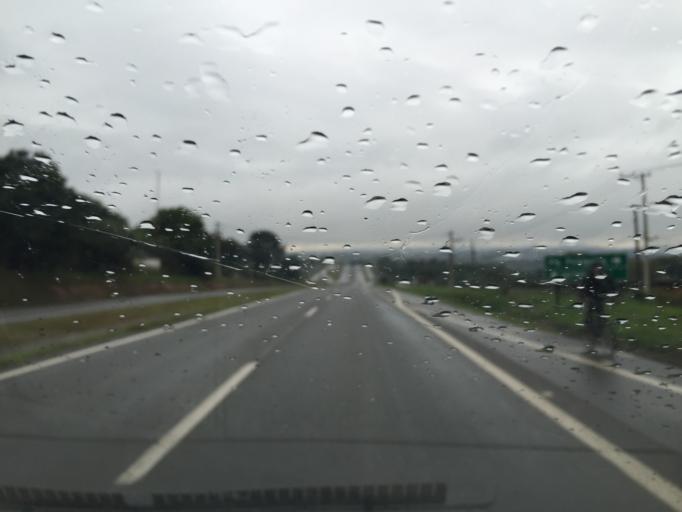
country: BR
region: Sao Paulo
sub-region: Itu
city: Itu
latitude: -23.2546
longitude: -47.3557
